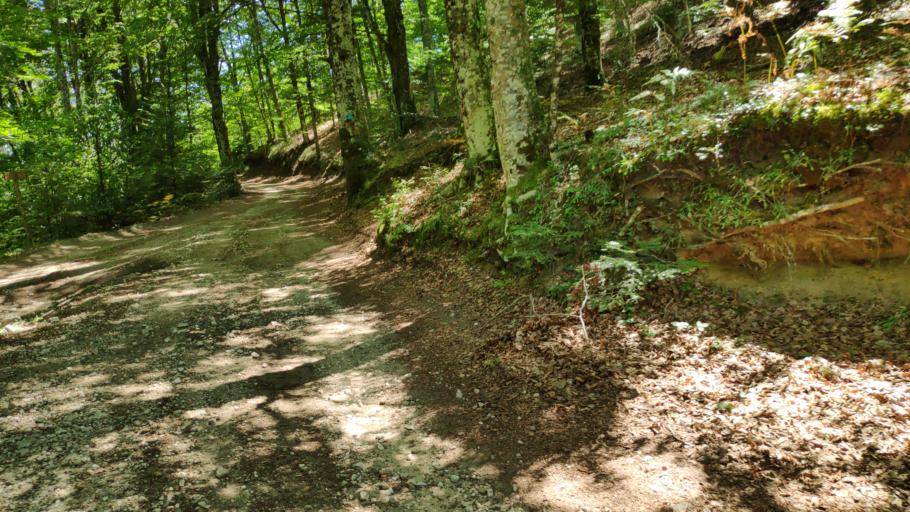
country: IT
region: Calabria
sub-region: Provincia di Vibo-Valentia
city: Serra San Bruno
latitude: 38.5382
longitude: 16.3808
